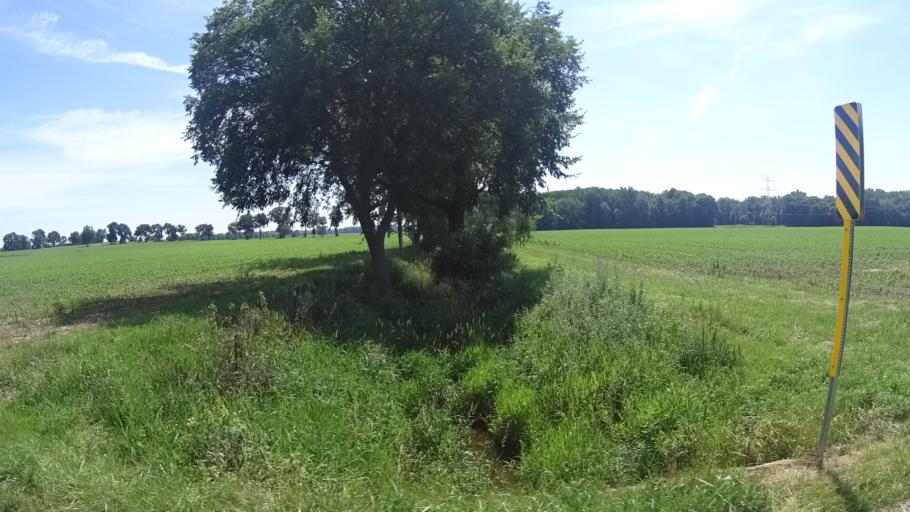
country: US
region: Ohio
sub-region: Huron County
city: Wakeman
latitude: 41.3390
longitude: -82.4388
